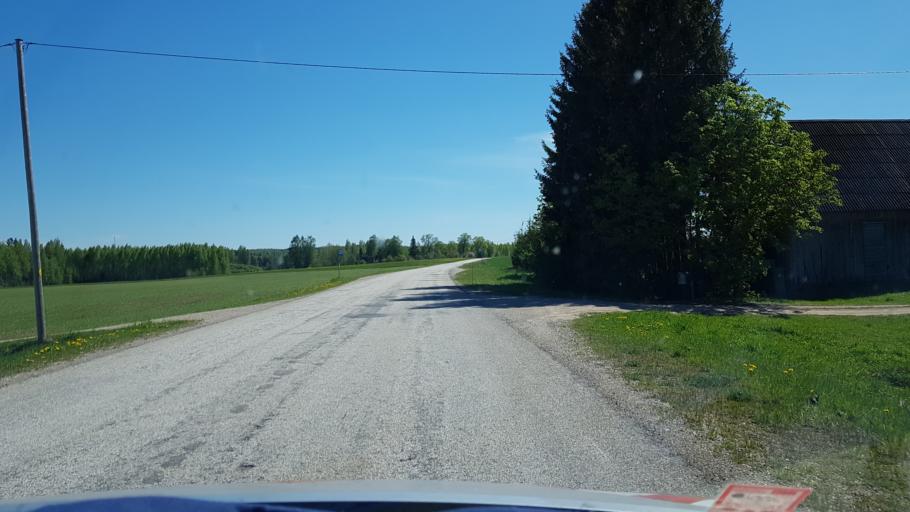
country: EE
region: Tartu
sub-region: UElenurme vald
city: Ulenurme
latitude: 58.2830
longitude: 26.9031
